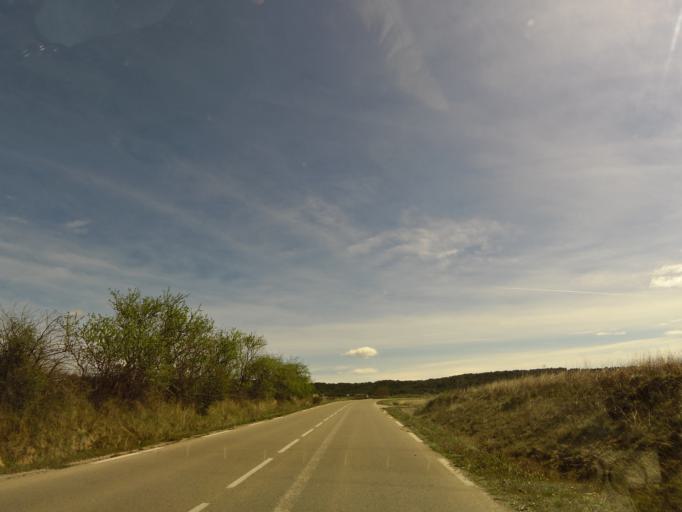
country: FR
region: Languedoc-Roussillon
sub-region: Departement du Gard
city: Langlade
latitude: 43.8160
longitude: 4.2387
